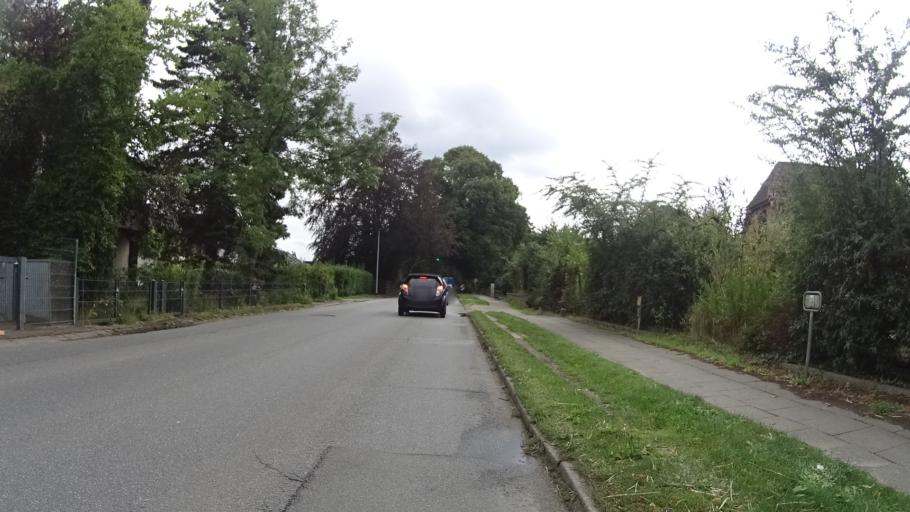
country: DE
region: Schleswig-Holstein
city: Tangstedt
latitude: 53.7323
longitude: 10.0886
